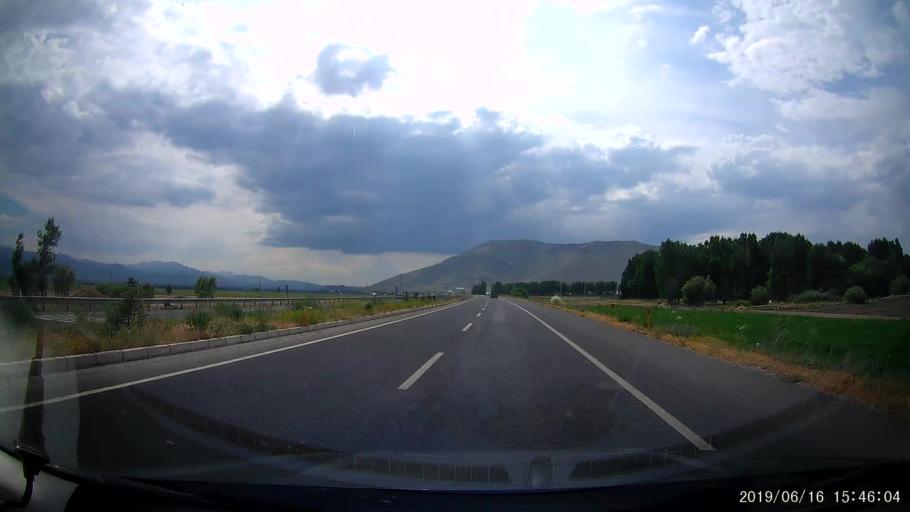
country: TR
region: Erzurum
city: Pasinler
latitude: 39.9899
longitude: 41.7523
